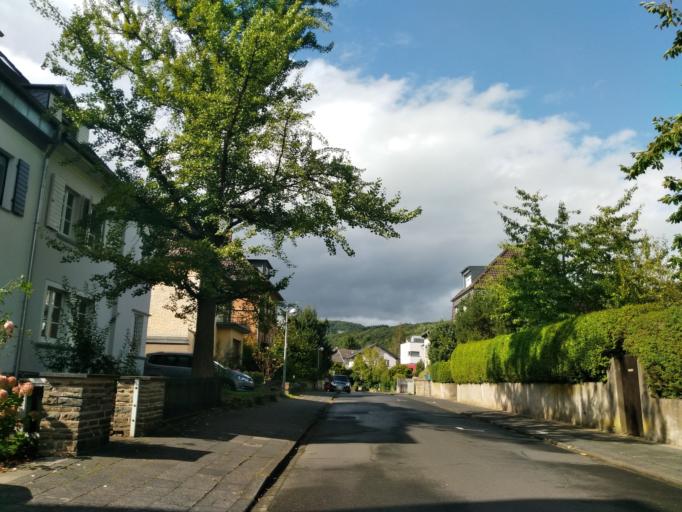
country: DE
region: North Rhine-Westphalia
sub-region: Regierungsbezirk Koln
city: Bad Honnef
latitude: 50.6494
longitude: 7.2287
